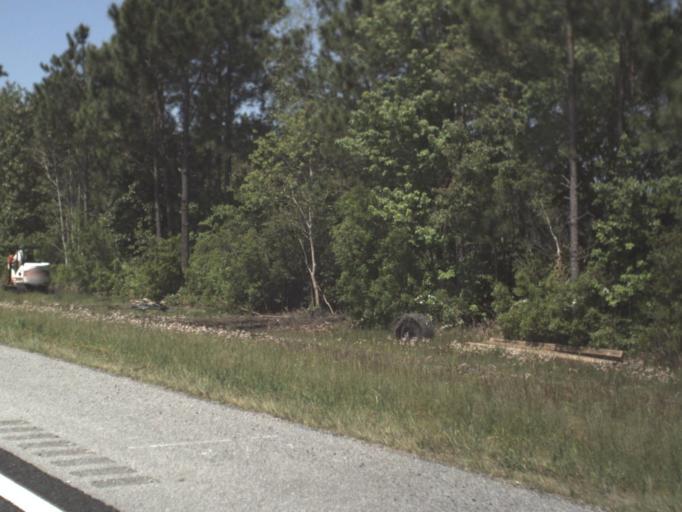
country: US
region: Florida
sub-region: Santa Rosa County
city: Bagdad
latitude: 30.5402
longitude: -87.0703
